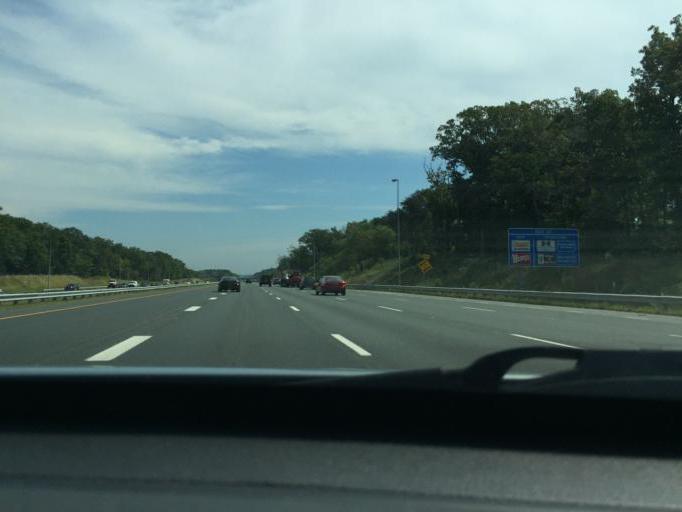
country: US
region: Virginia
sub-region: Prince William County
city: Linton Hall
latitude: 38.7984
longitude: -77.5627
